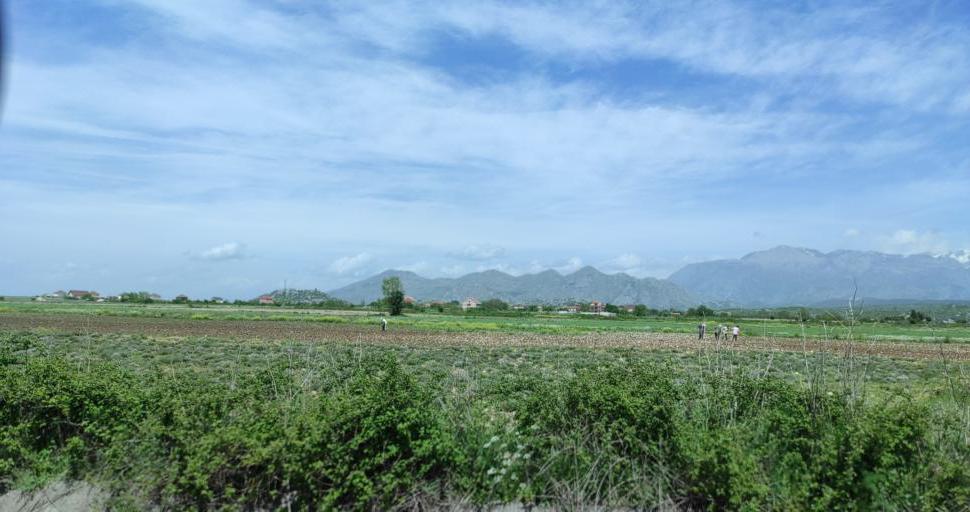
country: AL
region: Shkoder
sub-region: Rrethi i Malesia e Madhe
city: Gruemire
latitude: 42.1425
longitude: 19.5128
